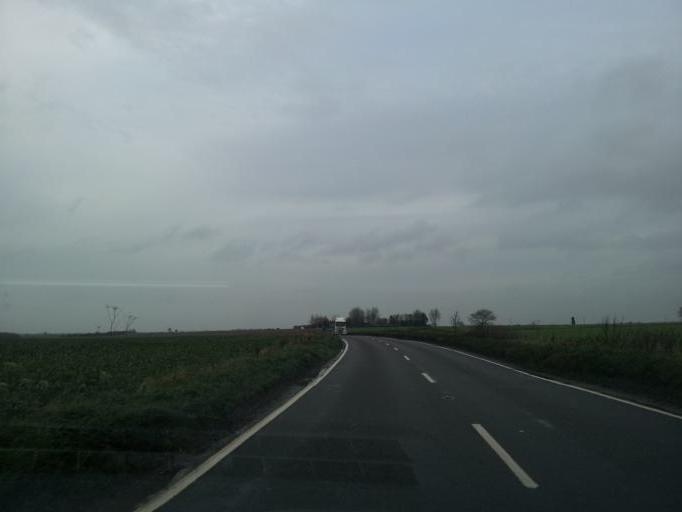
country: GB
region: England
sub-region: Norfolk
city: Martham
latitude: 52.6802
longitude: 1.5947
